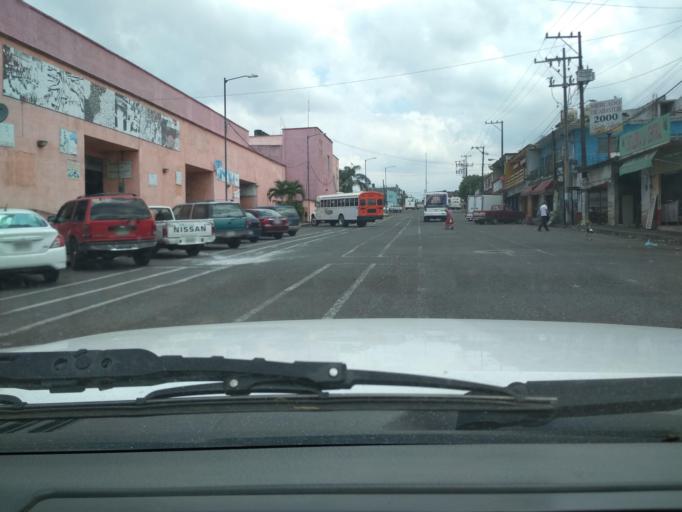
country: MX
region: Veracruz
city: Cordoba
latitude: 18.8857
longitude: -96.9206
